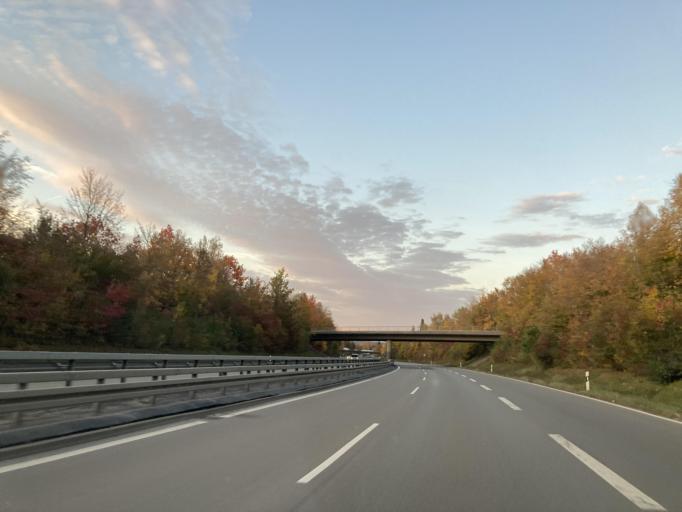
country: DE
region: Baden-Wuerttemberg
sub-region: Tuebingen Region
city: Balingen
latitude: 48.2718
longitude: 8.8582
